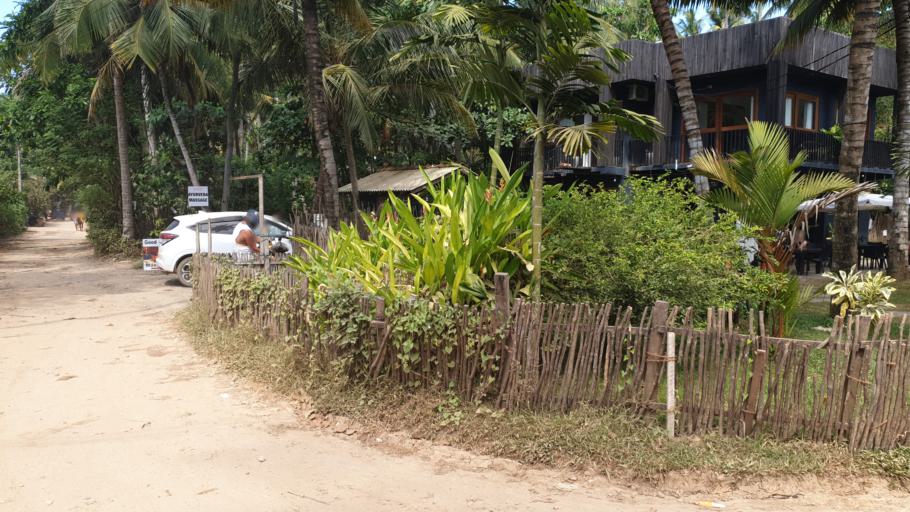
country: LK
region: Southern
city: Tangalla
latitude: 5.9626
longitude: 80.7067
